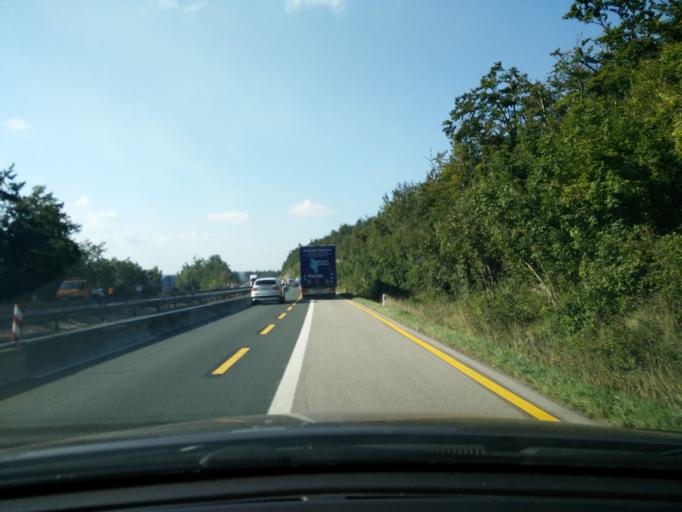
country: SI
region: Cerknica
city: Rakek
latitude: 45.8427
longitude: 14.2917
